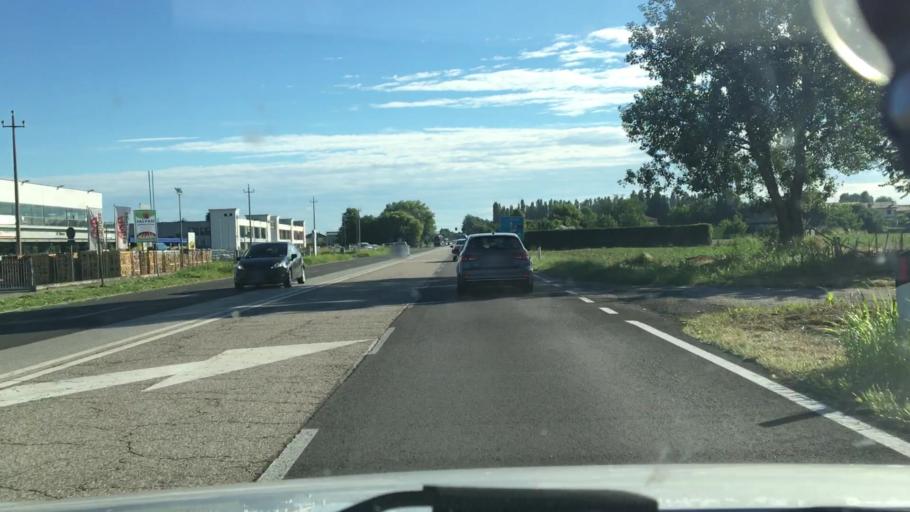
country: IT
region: Veneto
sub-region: Provincia di Rovigo
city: Rovigo
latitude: 45.0417
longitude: 11.7843
